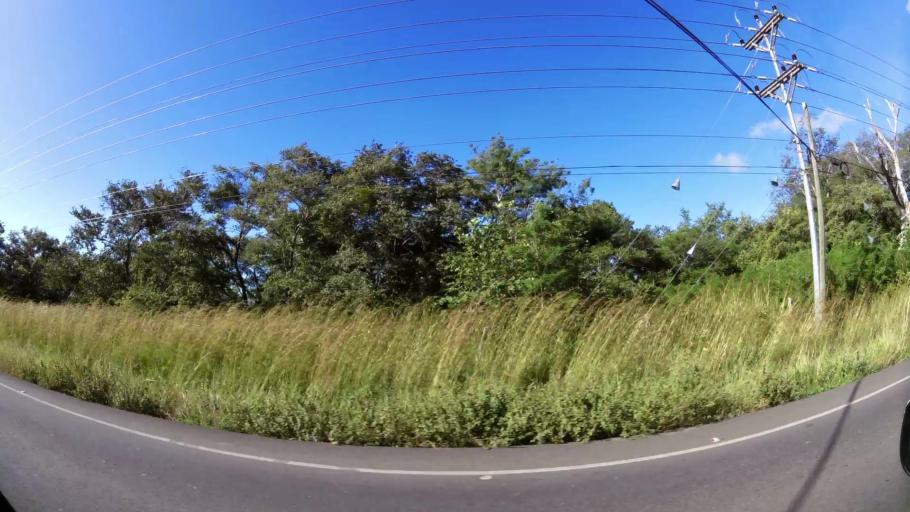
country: CR
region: Guanacaste
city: Sardinal
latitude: 10.3749
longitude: -85.7838
